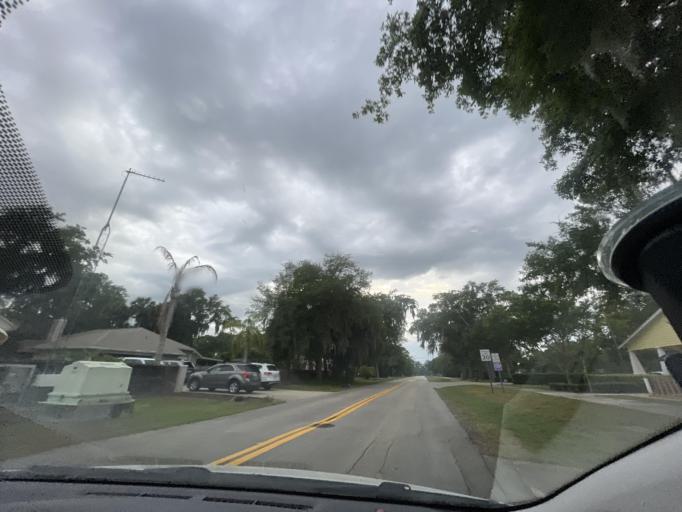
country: US
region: Florida
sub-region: Volusia County
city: Port Orange
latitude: 29.0924
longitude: -80.9932
